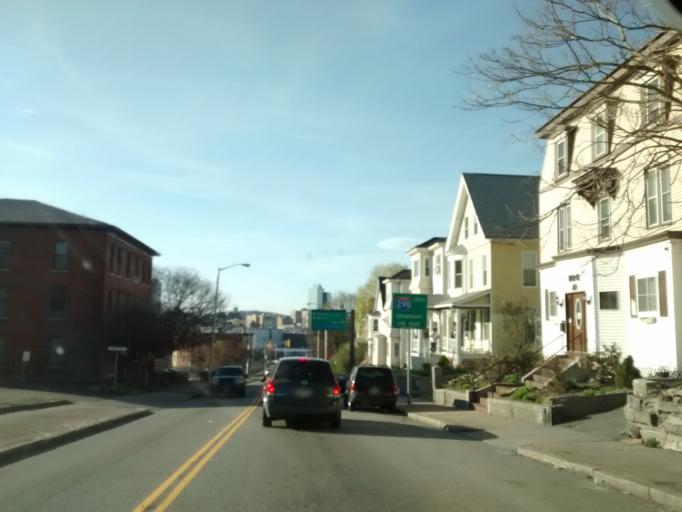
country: US
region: Massachusetts
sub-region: Worcester County
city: Worcester
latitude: 42.2527
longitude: -71.7963
